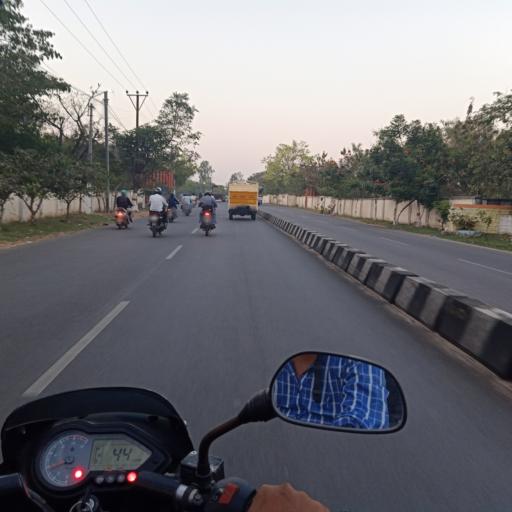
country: IN
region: Telangana
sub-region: Hyderabad
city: Malkajgiri
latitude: 17.4808
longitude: 78.5111
